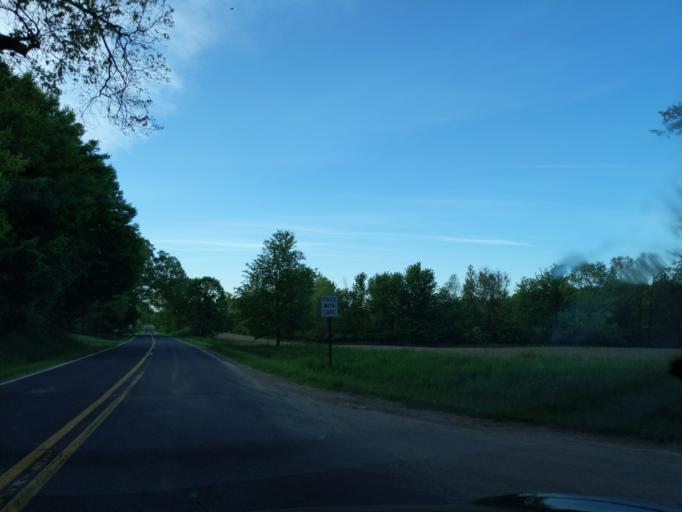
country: US
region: Michigan
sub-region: Ingham County
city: Stockbridge
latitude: 42.5270
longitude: -84.3026
